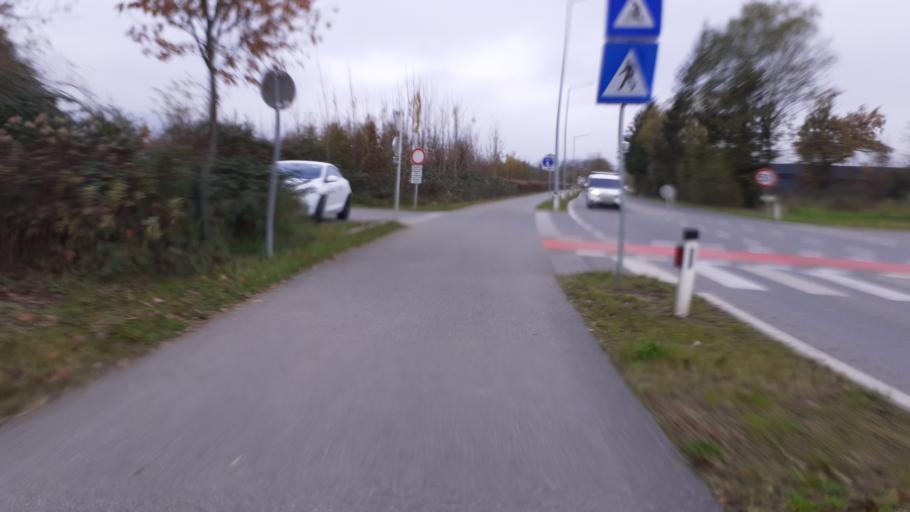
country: AT
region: Vorarlberg
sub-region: Politischer Bezirk Feldkirch
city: Nofels
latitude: 47.2663
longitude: 9.5913
